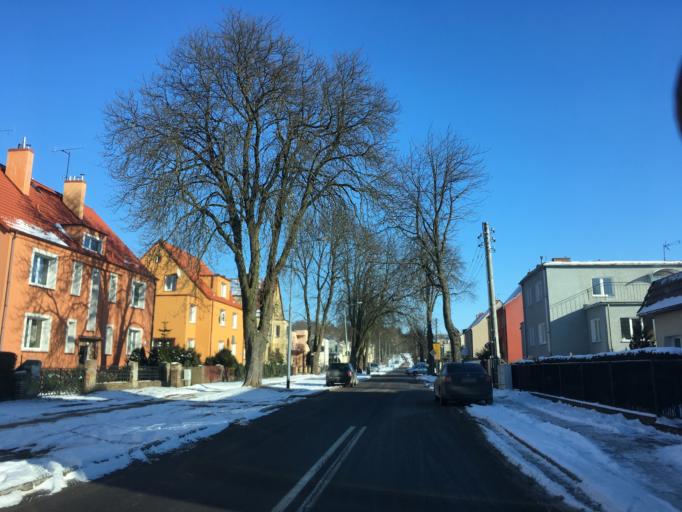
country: PL
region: Pomeranian Voivodeship
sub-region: Slupsk
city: Slupsk
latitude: 54.4591
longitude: 17.0430
